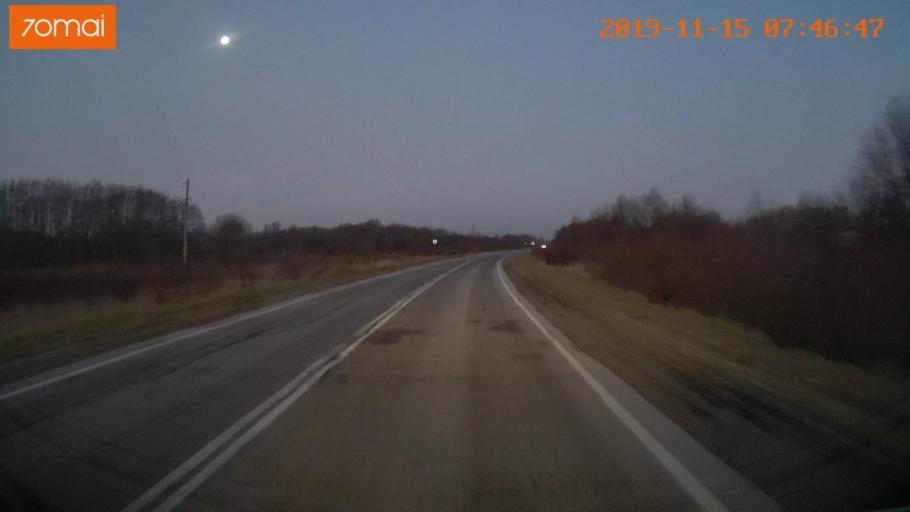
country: RU
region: Vologda
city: Sheksna
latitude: 58.8354
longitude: 38.2738
